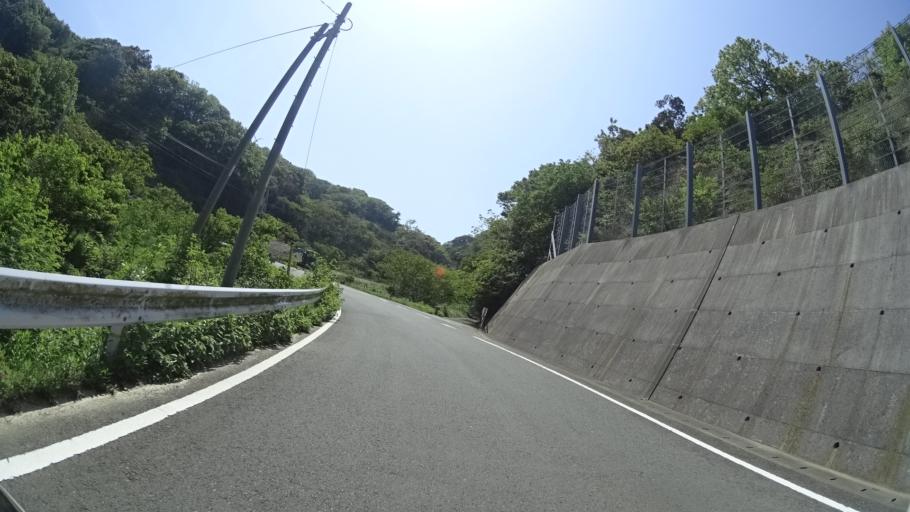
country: JP
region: Oita
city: Tsukumiura
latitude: 33.3594
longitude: 132.0385
